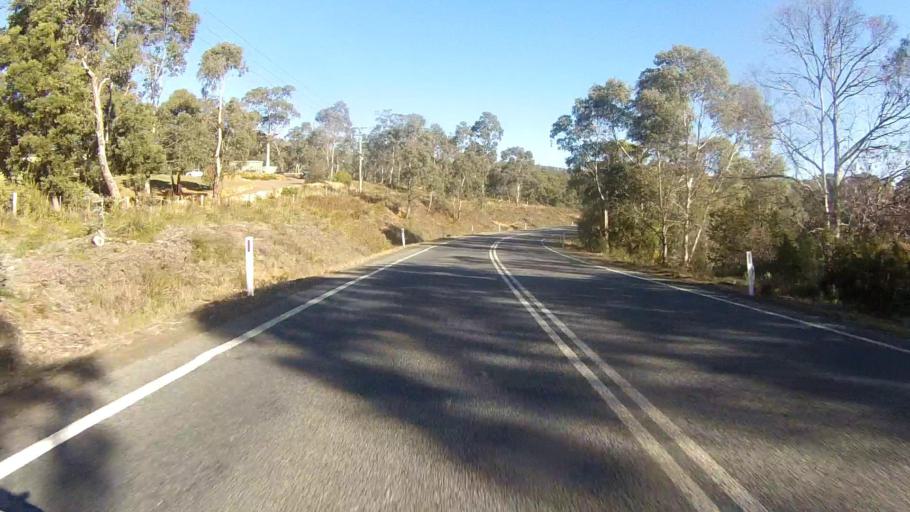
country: AU
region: Tasmania
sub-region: Clarence
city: Sandford
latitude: -43.0225
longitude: 147.8980
